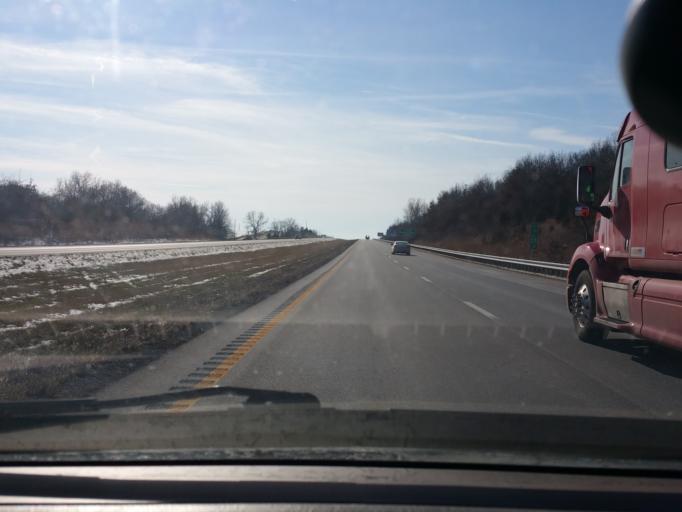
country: US
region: Missouri
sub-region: Clinton County
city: Cameron
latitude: 39.7706
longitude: -94.2137
